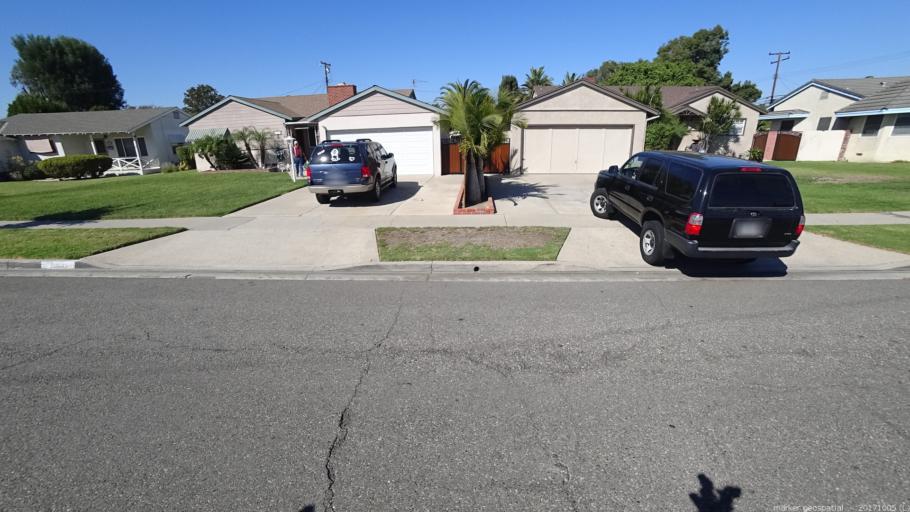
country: US
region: California
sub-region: Orange County
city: Garden Grove
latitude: 33.7855
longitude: -117.9464
